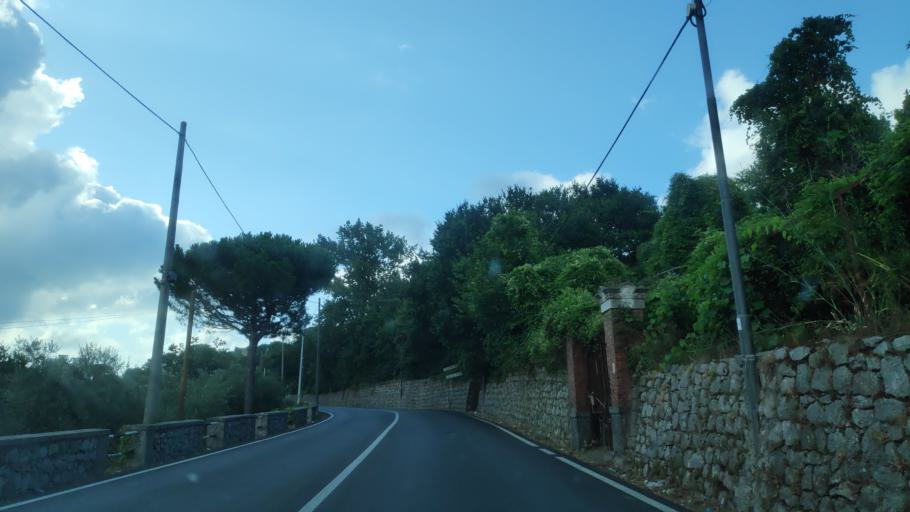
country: IT
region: Campania
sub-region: Provincia di Napoli
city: Piano di Sorrento
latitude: 40.6189
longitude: 14.4242
